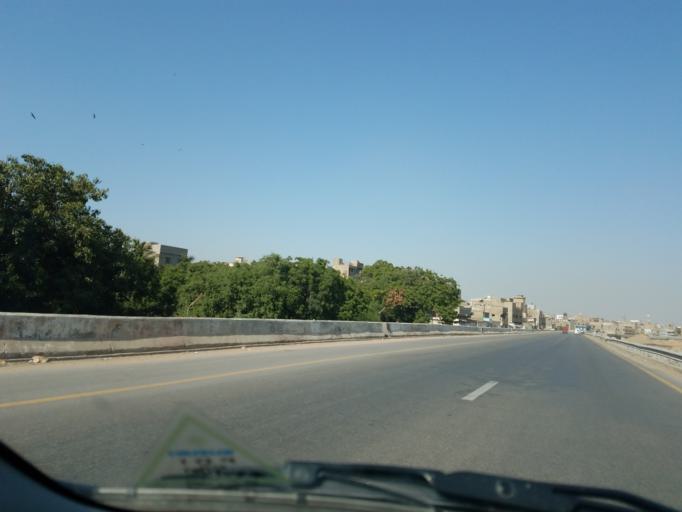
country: PK
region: Sindh
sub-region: Karachi District
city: Karachi
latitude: 24.8868
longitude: 67.0236
